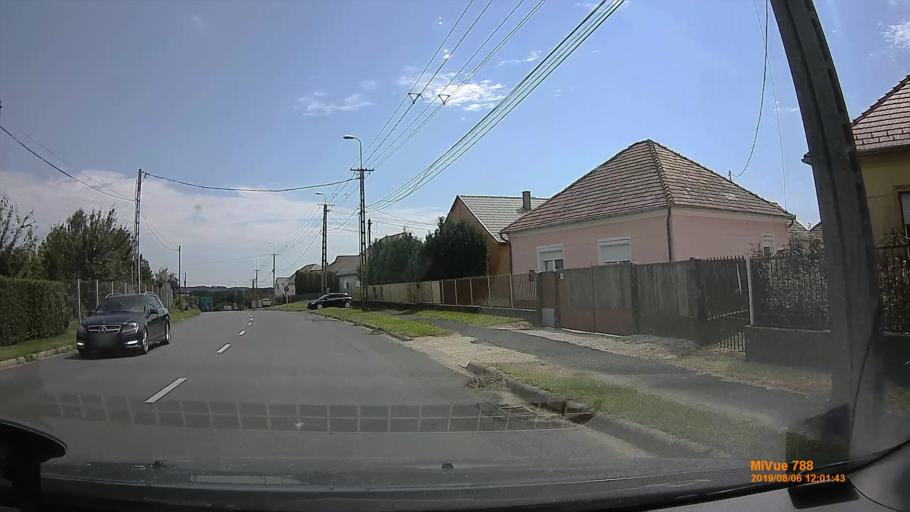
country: HU
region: Zala
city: Becsehely
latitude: 46.4508
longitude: 16.8072
